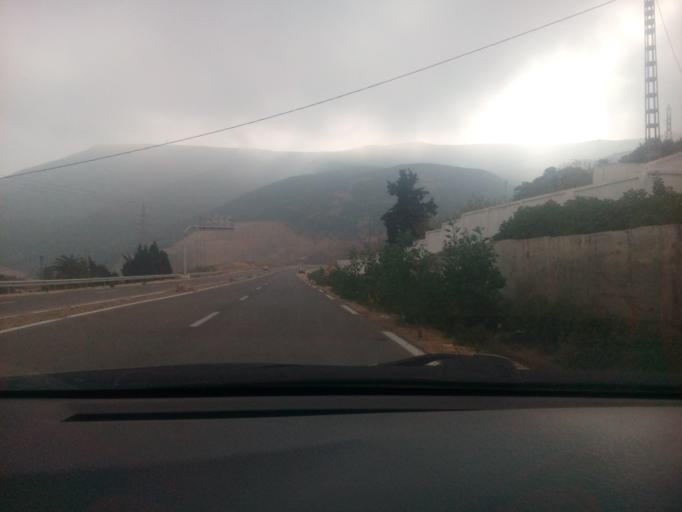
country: DZ
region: Oran
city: Mers el Kebir
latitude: 35.7210
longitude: -0.7328
